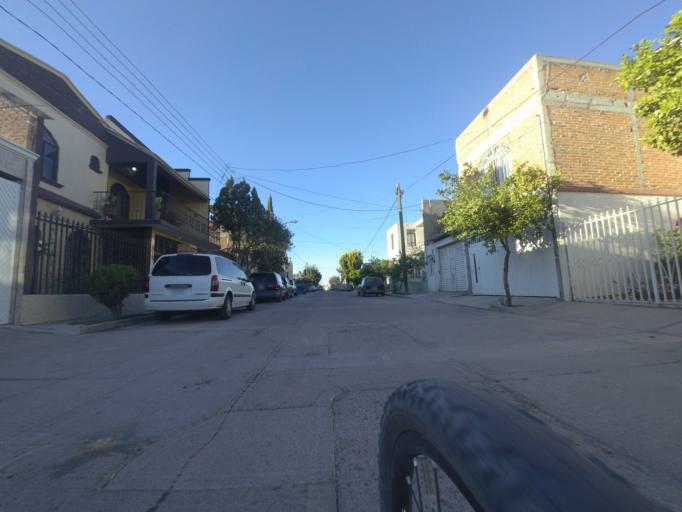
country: MX
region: Aguascalientes
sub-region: Aguascalientes
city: La Loma de los Negritos
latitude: 21.8505
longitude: -102.3399
